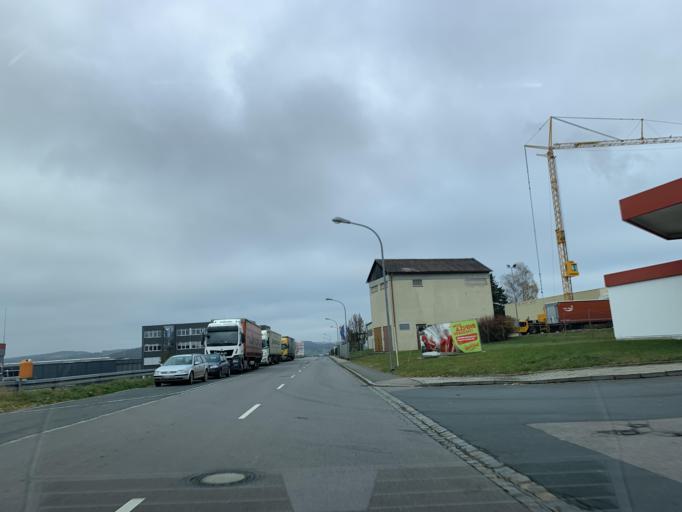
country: DE
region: Bavaria
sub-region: Upper Palatinate
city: Neunburg vorm Wald
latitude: 49.3374
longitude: 12.4014
